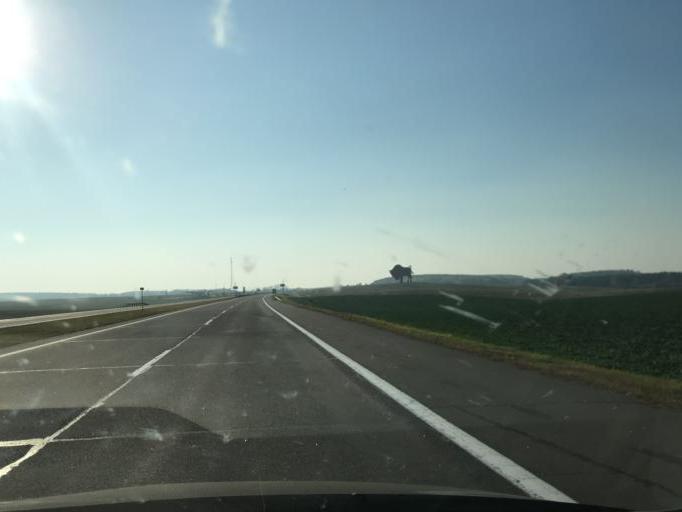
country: BY
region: Minsk
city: Snow
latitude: 53.3022
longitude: 26.3778
